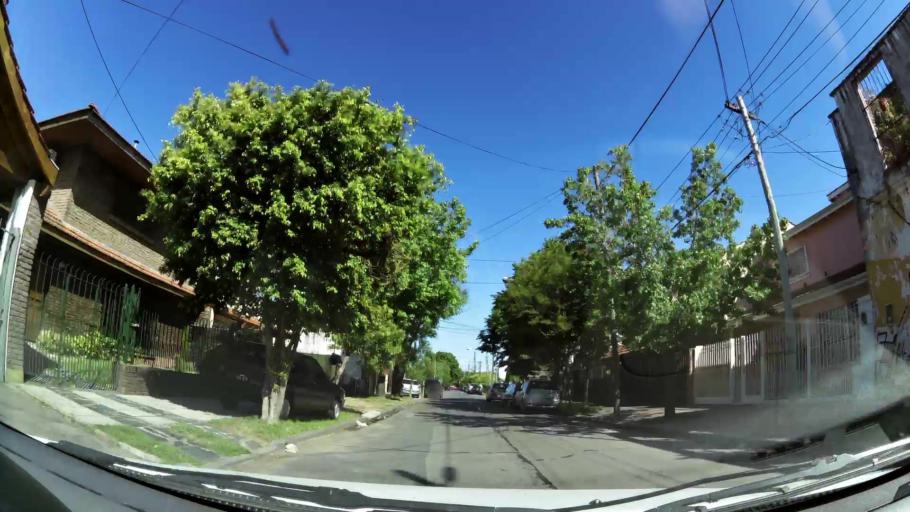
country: AR
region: Buenos Aires
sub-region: Partido de San Isidro
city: San Isidro
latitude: -34.5081
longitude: -58.5699
